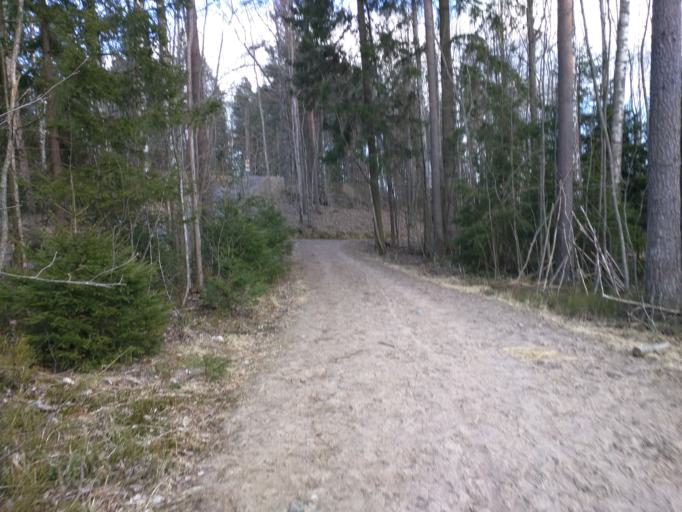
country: FI
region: Uusimaa
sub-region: Helsinki
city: Kilo
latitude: 60.2290
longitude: 24.7880
